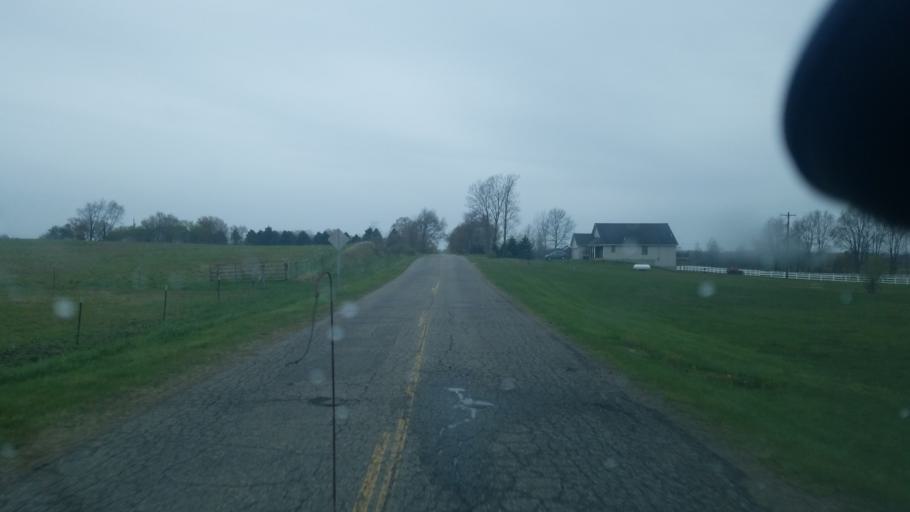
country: US
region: Michigan
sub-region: Montcalm County
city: Lakeview
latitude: 43.5110
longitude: -85.2864
